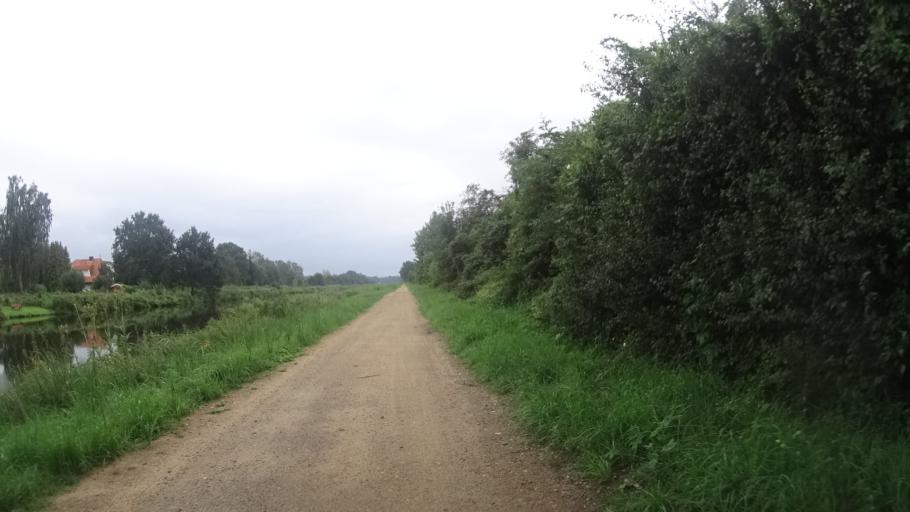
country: DE
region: Schleswig-Holstein
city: Witzeeze
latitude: 53.4468
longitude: 10.6204
